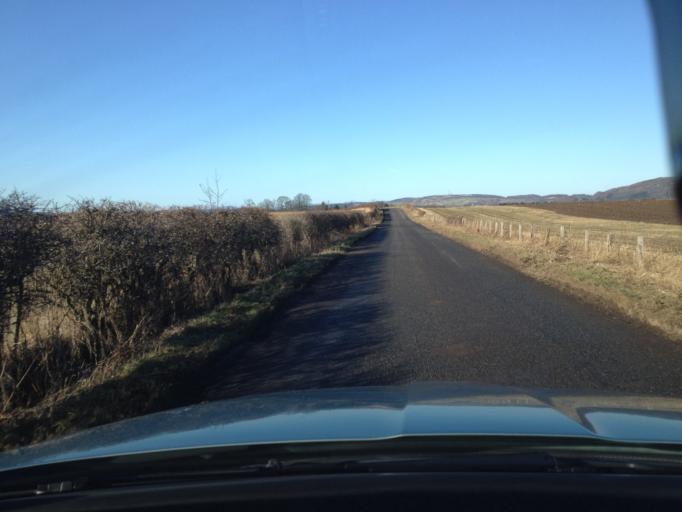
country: GB
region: Scotland
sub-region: Perth and Kinross
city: Bridge of Earn
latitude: 56.3300
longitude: -3.3824
